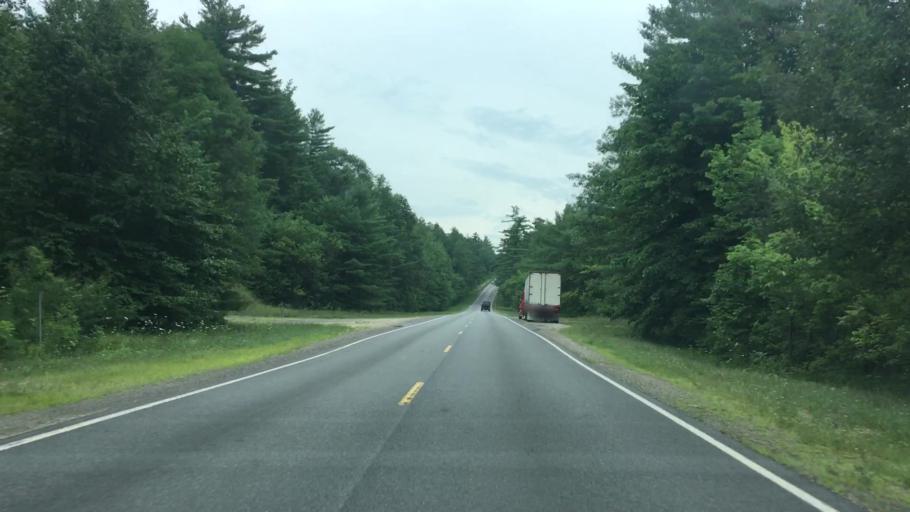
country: US
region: New York
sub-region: Clinton County
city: Peru
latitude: 44.4952
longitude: -73.5923
